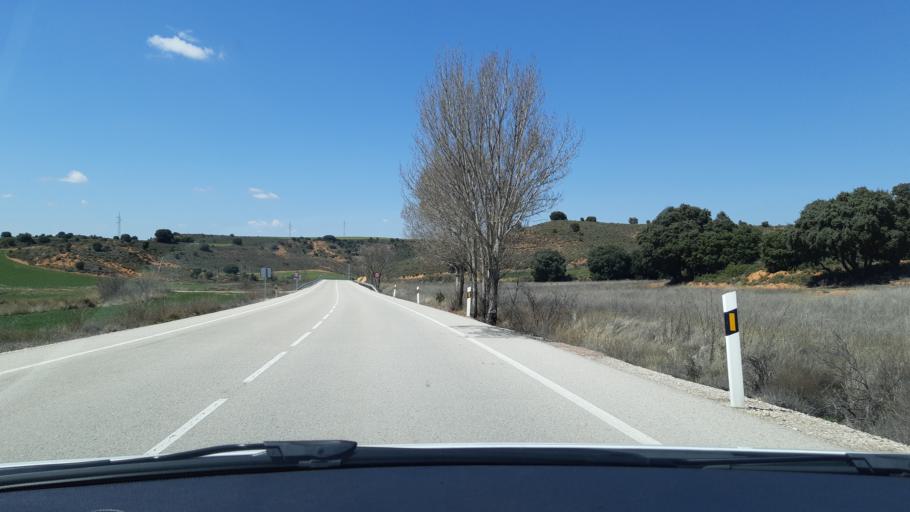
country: ES
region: Castille-La Mancha
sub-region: Provincia de Guadalajara
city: Masegoso de Tajuna
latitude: 40.8026
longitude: -2.6651
